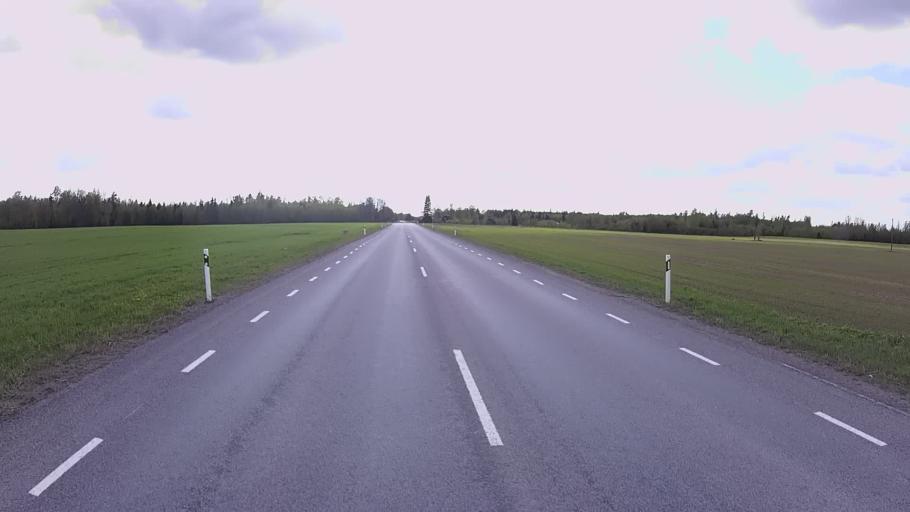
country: EE
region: Tartu
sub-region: Alatskivi vald
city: Kallaste
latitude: 58.5161
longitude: 26.9945
